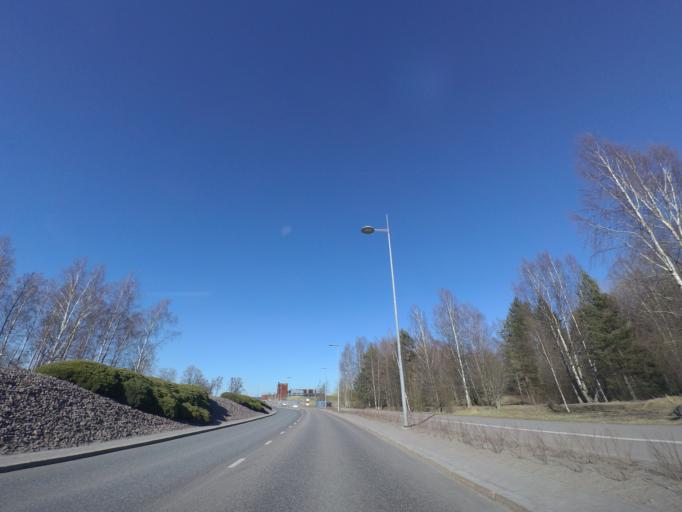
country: FI
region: Uusimaa
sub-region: Helsinki
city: Vantaa
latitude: 60.2091
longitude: 25.1605
